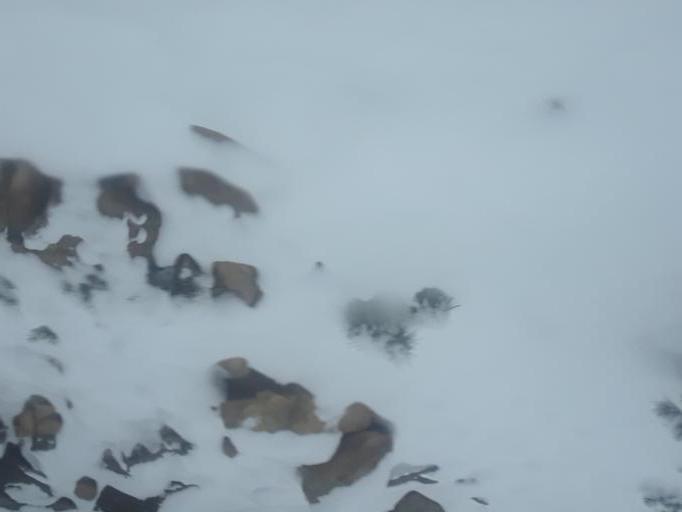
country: US
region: Colorado
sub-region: Boulder County
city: Coal Creek
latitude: 39.9204
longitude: -105.3766
